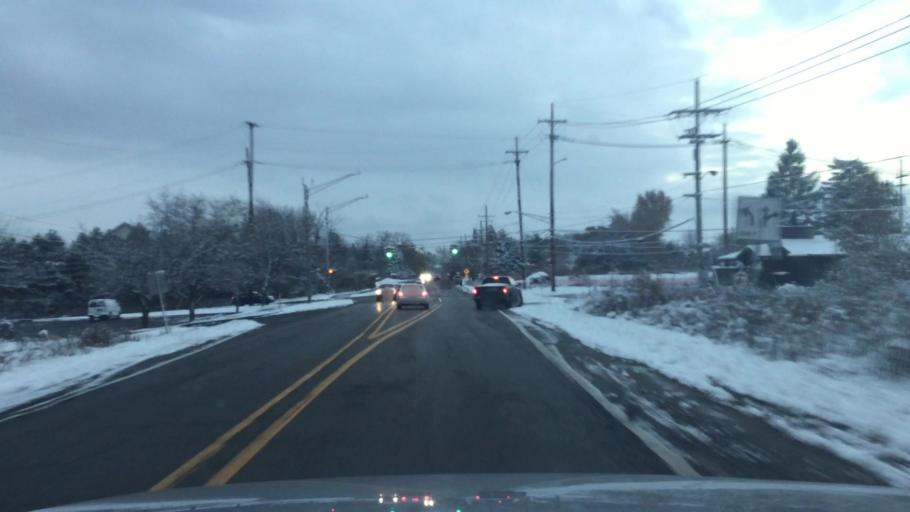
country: US
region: Michigan
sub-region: Oakland County
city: West Bloomfield Township
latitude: 42.6084
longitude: -83.3983
